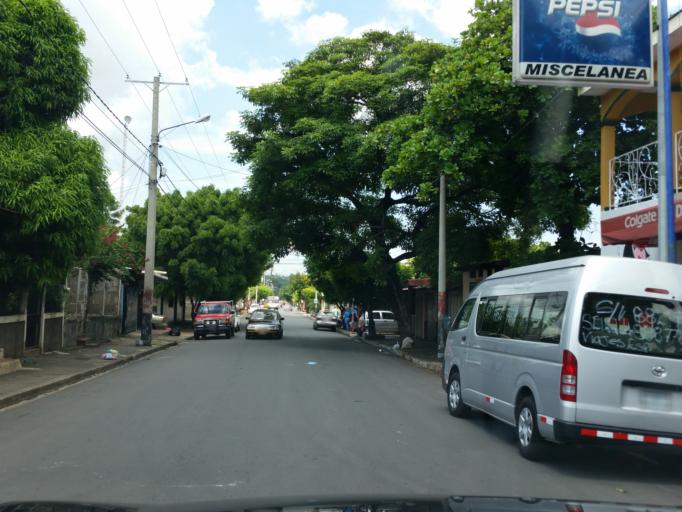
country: NI
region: Managua
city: Managua
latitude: 12.1390
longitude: -86.2558
